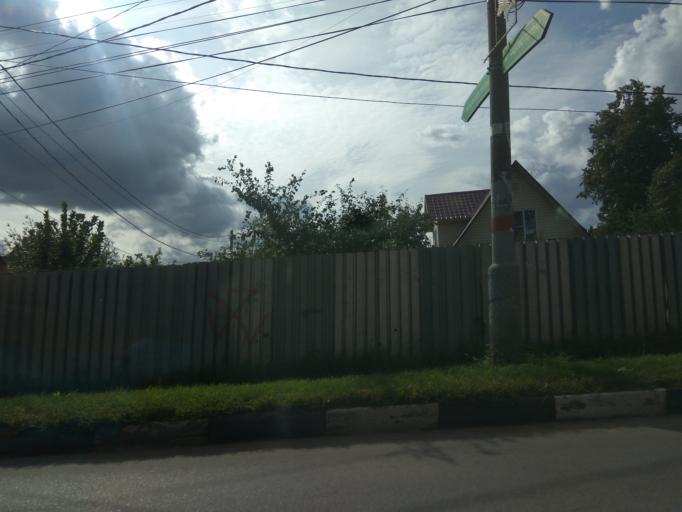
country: RU
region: Moskovskaya
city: Malakhovka
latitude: 55.6416
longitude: 38.0098
